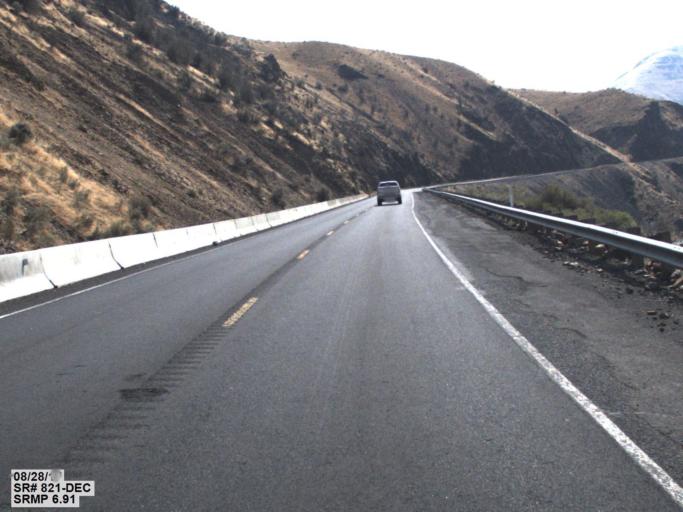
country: US
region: Washington
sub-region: Yakima County
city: Selah
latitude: 46.7611
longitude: -120.4529
